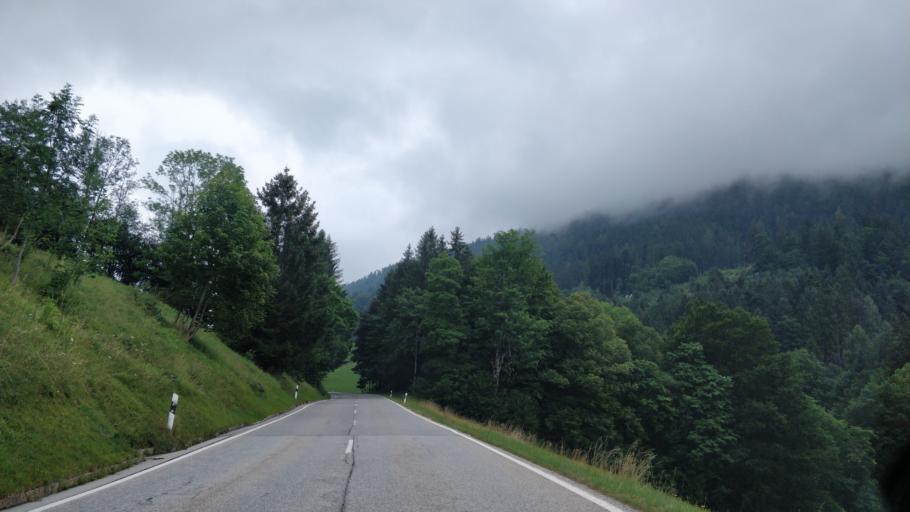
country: AT
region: Salzburg
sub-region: Politischer Bezirk Hallein
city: Hallein
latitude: 47.6548
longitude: 13.0778
